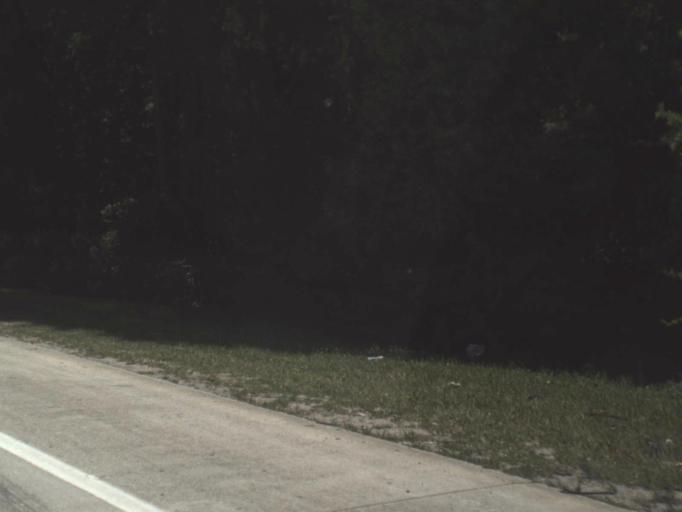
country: US
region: Florida
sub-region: Saint Johns County
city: Fruit Cove
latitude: 30.1922
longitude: -81.5570
